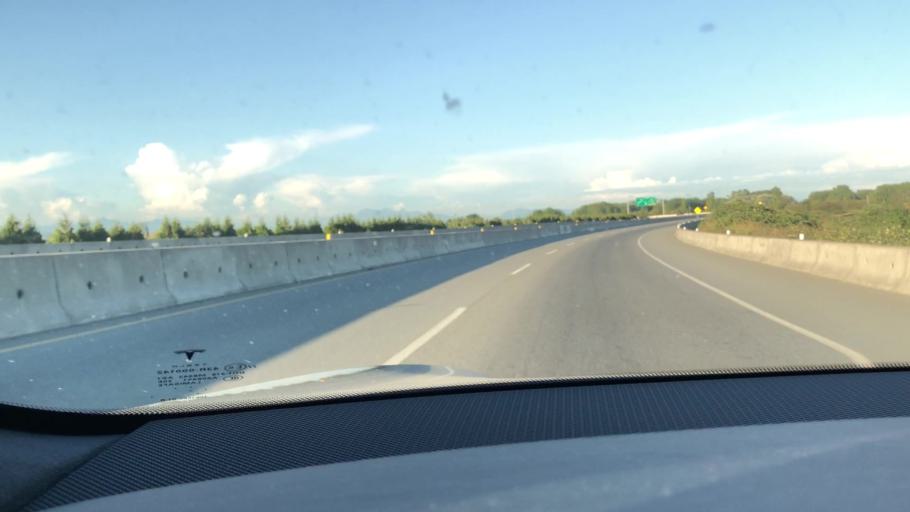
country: CA
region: British Columbia
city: Ladner
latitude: 49.0815
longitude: -123.0321
